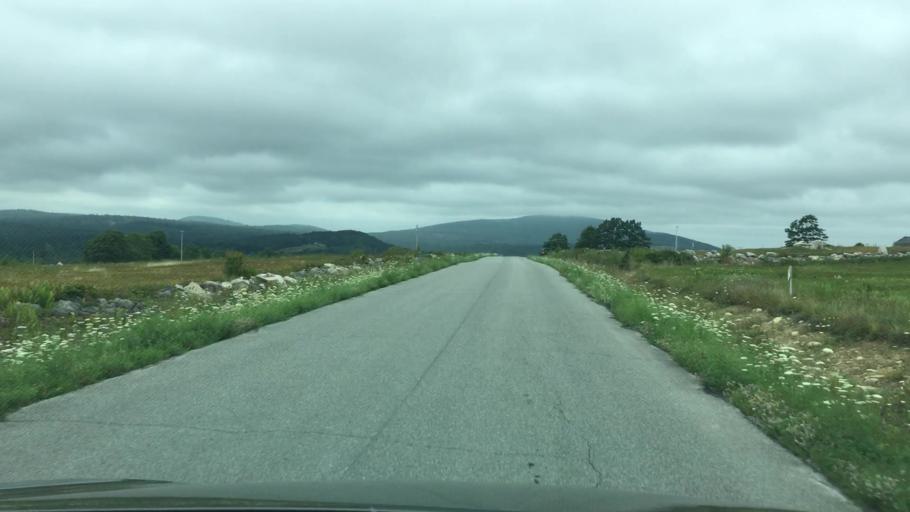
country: US
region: Maine
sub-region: Waldo County
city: Stockton Springs
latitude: 44.5233
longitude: -68.8813
